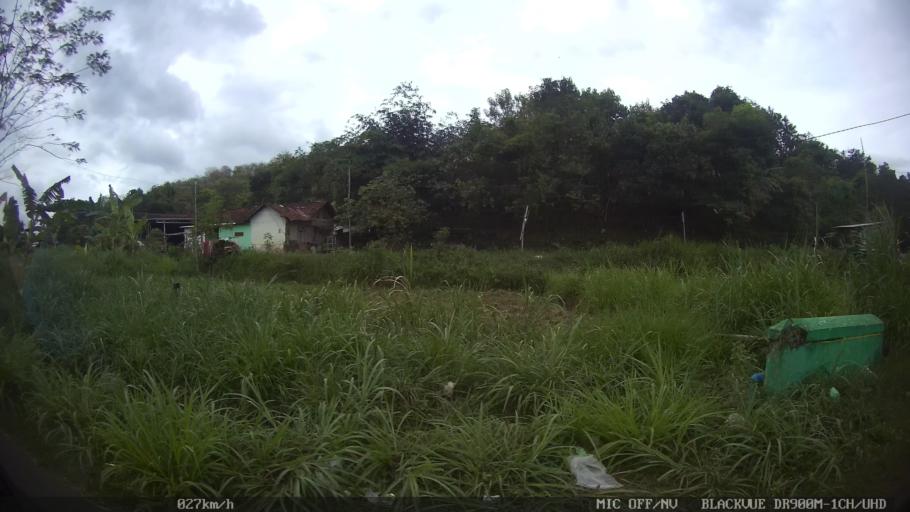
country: ID
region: Daerah Istimewa Yogyakarta
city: Sewon
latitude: -7.8632
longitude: 110.4211
